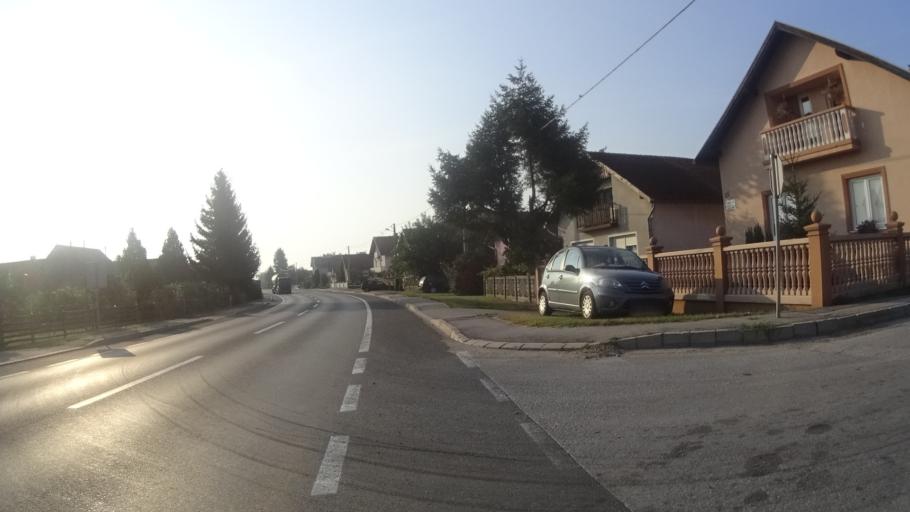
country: HR
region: Varazdinska
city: Sracinec
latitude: 46.3366
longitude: 16.2535
